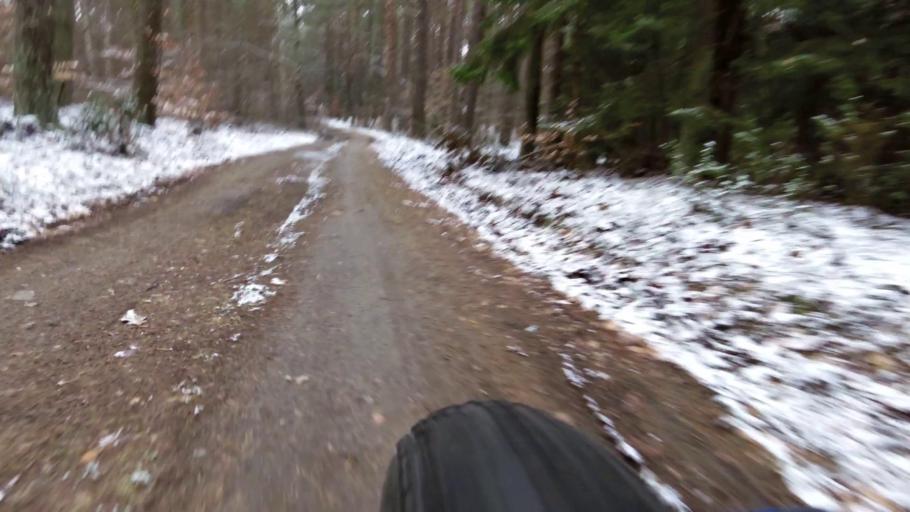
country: PL
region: West Pomeranian Voivodeship
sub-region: Powiat walecki
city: Miroslawiec
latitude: 53.3045
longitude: 16.0663
